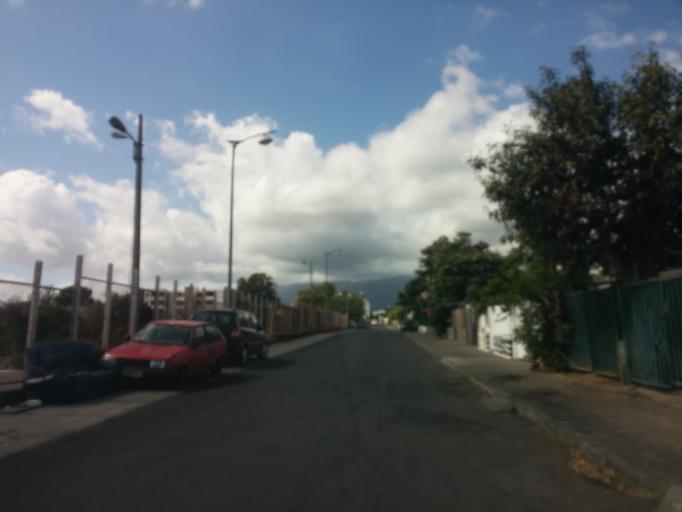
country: RE
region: Reunion
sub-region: Reunion
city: Le Port
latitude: -20.9418
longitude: 55.2869
